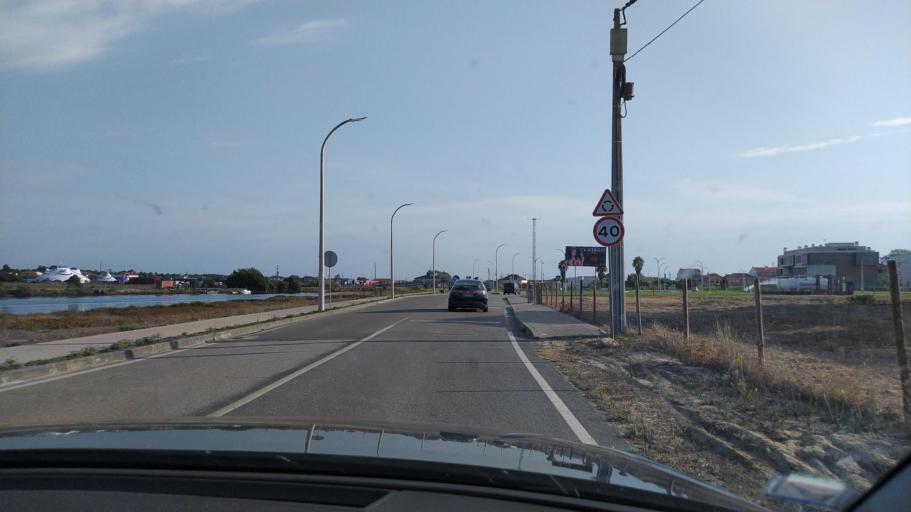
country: PT
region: Aveiro
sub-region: Ilhavo
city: Gafanha da Encarnacao
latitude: 40.5637
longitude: -8.7572
